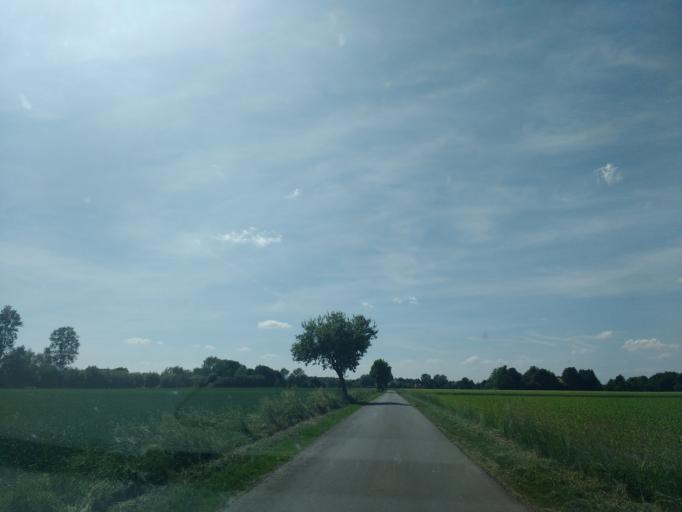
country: DE
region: North Rhine-Westphalia
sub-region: Regierungsbezirk Detmold
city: Paderborn
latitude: 51.7236
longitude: 8.6797
